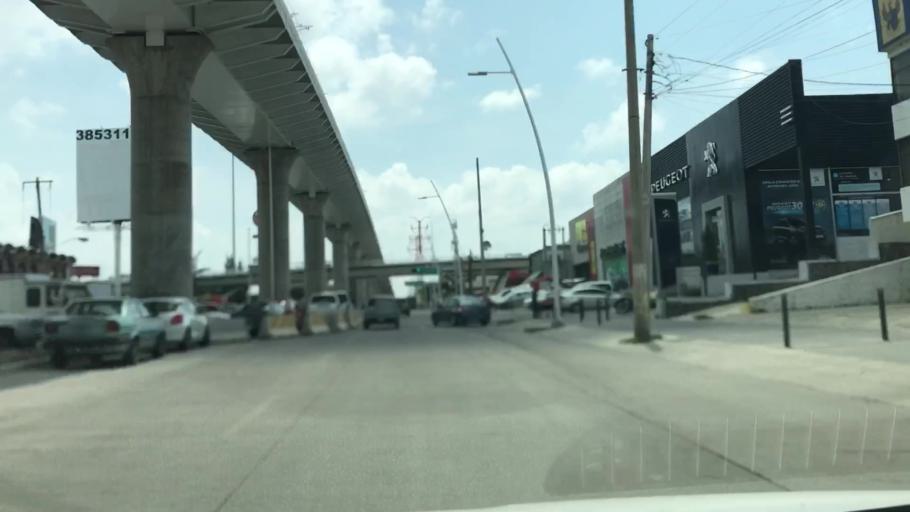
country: MX
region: Jalisco
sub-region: Zapopan
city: Zapopan
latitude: 20.7063
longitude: -103.3658
